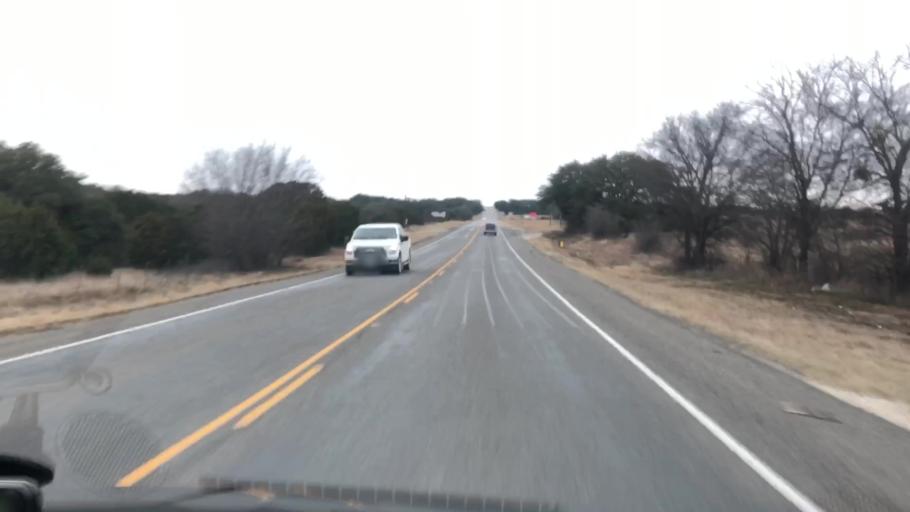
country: US
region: Texas
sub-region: Hamilton County
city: Hico
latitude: 31.9957
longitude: -98.0464
